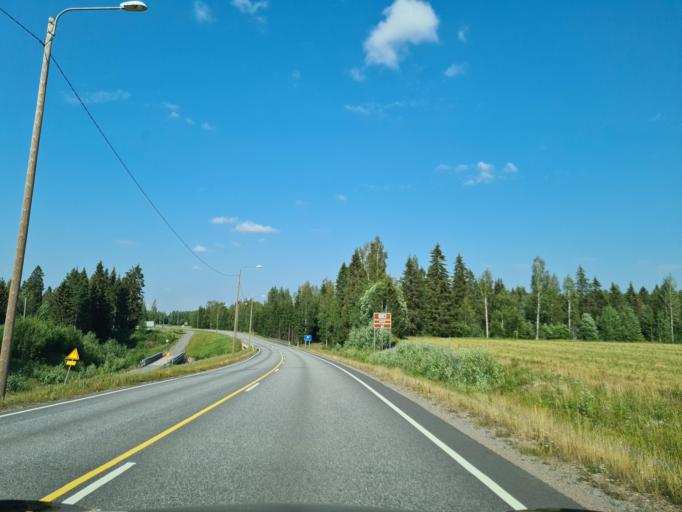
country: FI
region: Satakunta
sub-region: Pohjois-Satakunta
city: Karvia
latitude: 62.0758
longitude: 22.5106
